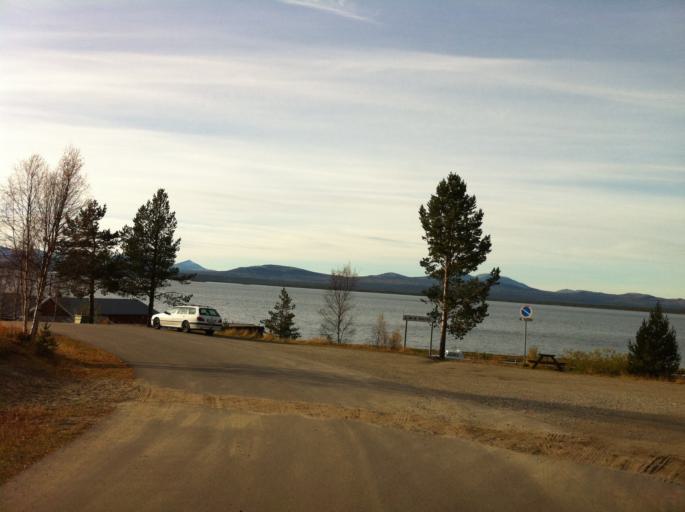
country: NO
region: Hedmark
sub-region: Engerdal
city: Engerdal
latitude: 62.1565
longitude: 11.9482
